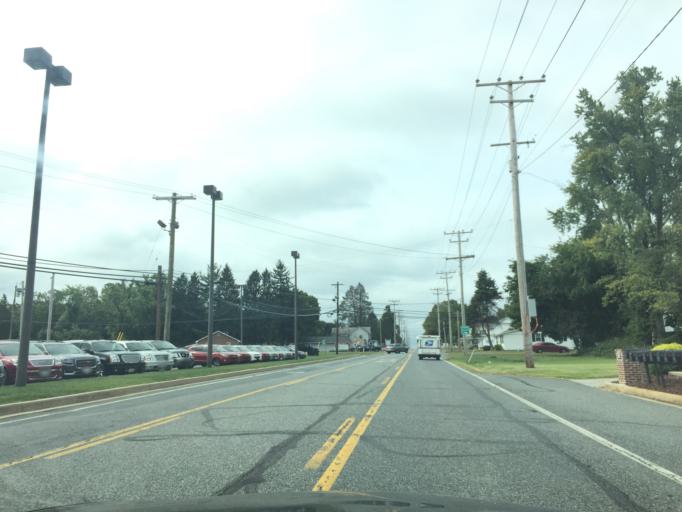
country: US
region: Maryland
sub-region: Harford County
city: Fallston
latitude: 39.5059
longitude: -76.3853
